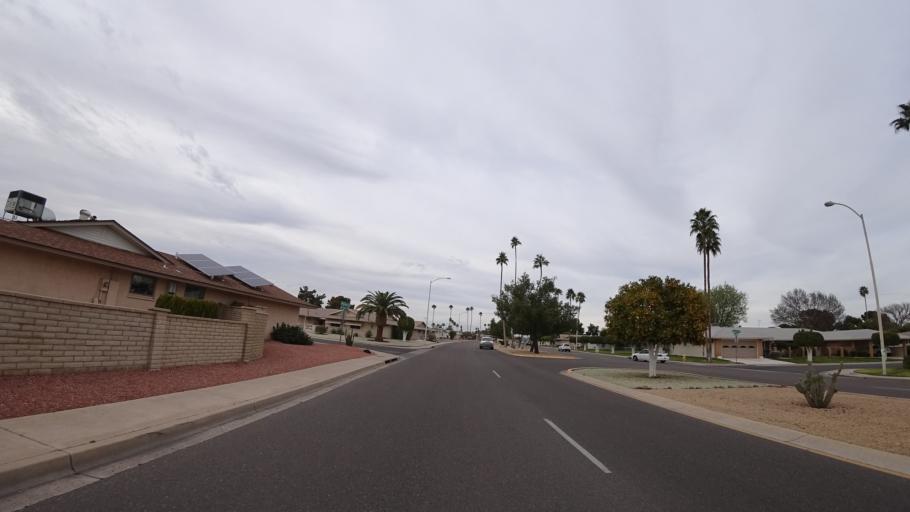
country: US
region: Arizona
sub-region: Maricopa County
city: Youngtown
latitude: 33.6131
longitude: -112.2905
